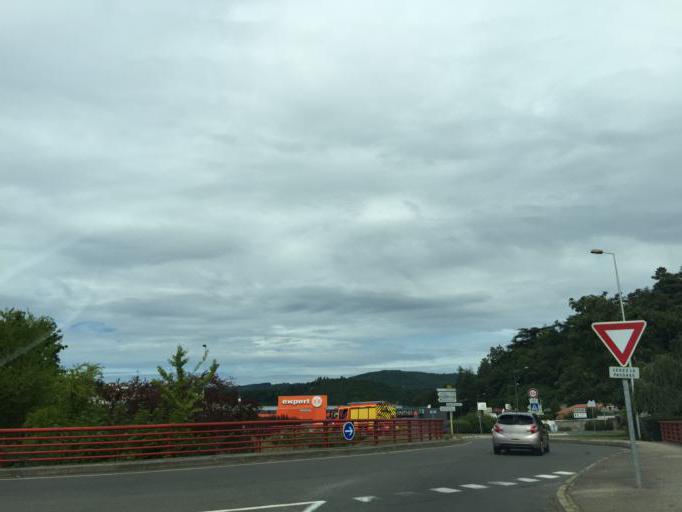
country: FR
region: Rhone-Alpes
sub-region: Departement de la Loire
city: Unieux
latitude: 45.3922
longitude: 4.2727
